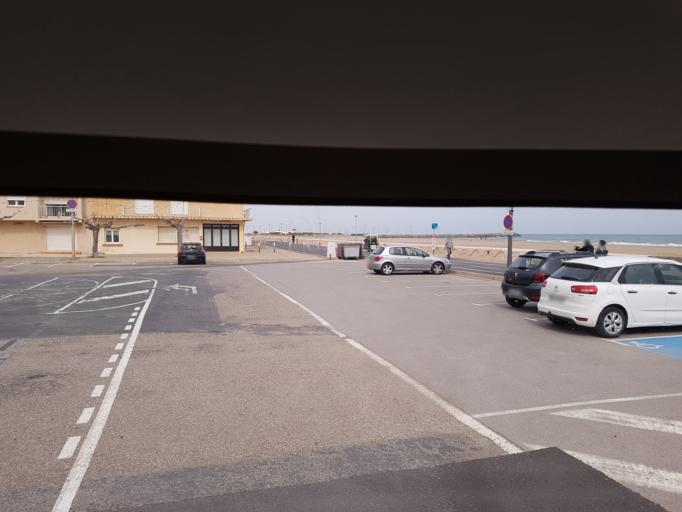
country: FR
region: Languedoc-Roussillon
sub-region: Departement de l'Aude
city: Fleury
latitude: 43.1665
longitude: 3.1765
